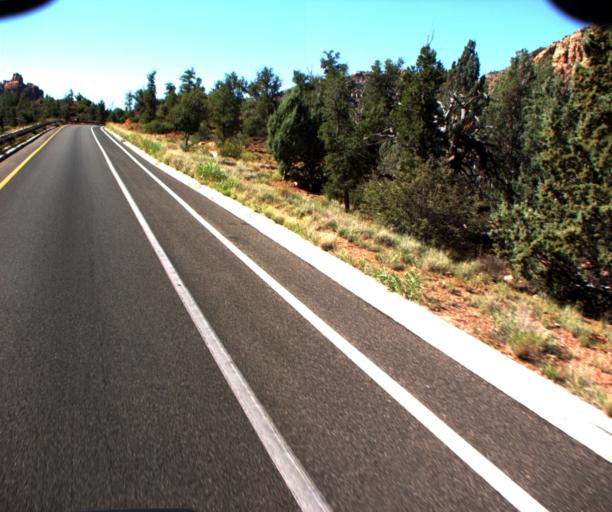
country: US
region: Arizona
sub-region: Yavapai County
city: Village of Oak Creek (Big Park)
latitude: 34.8144
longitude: -111.7690
